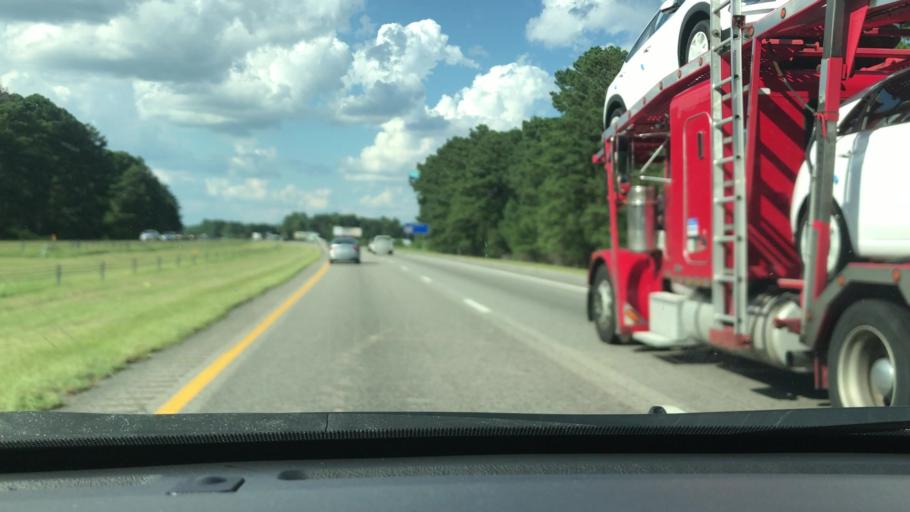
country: US
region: South Carolina
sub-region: Florence County
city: Timmonsville
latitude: 33.9587
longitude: -80.0467
